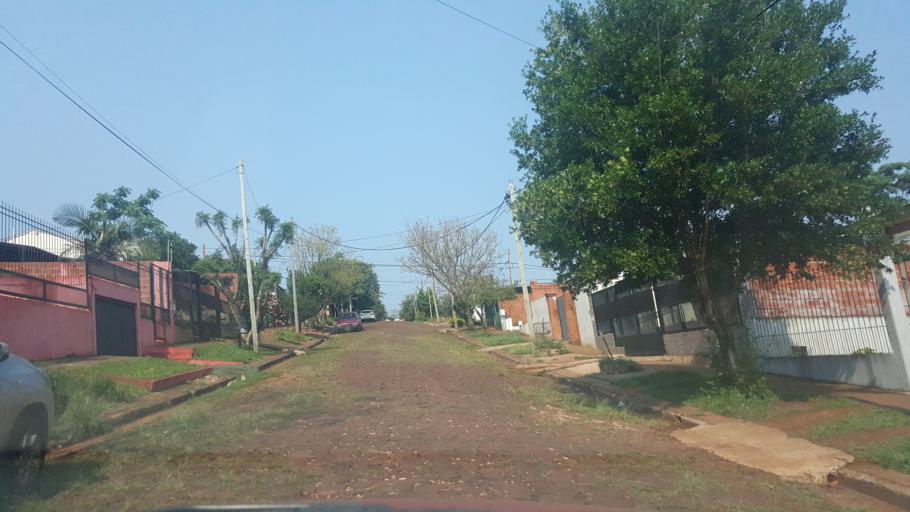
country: AR
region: Misiones
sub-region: Departamento de Capital
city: Posadas
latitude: -27.4181
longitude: -55.9551
